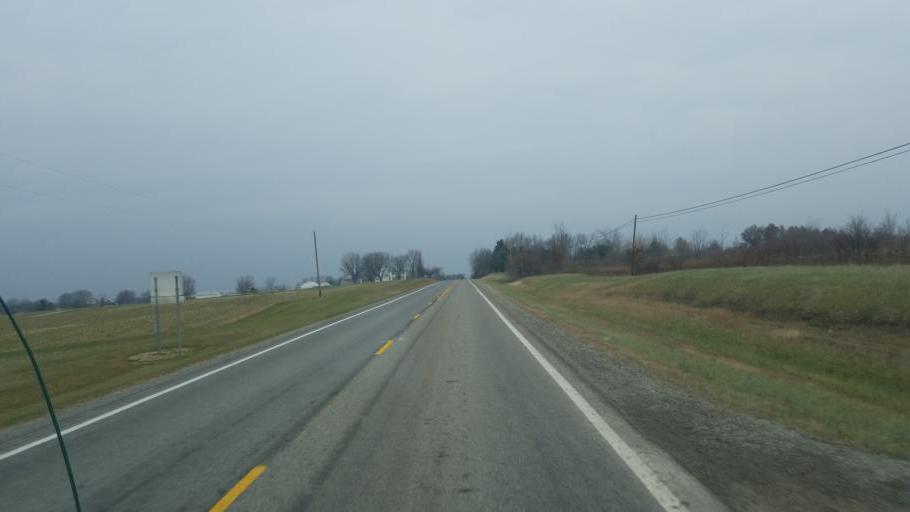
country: US
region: Ohio
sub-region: Crawford County
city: Galion
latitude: 40.6546
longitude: -82.8219
